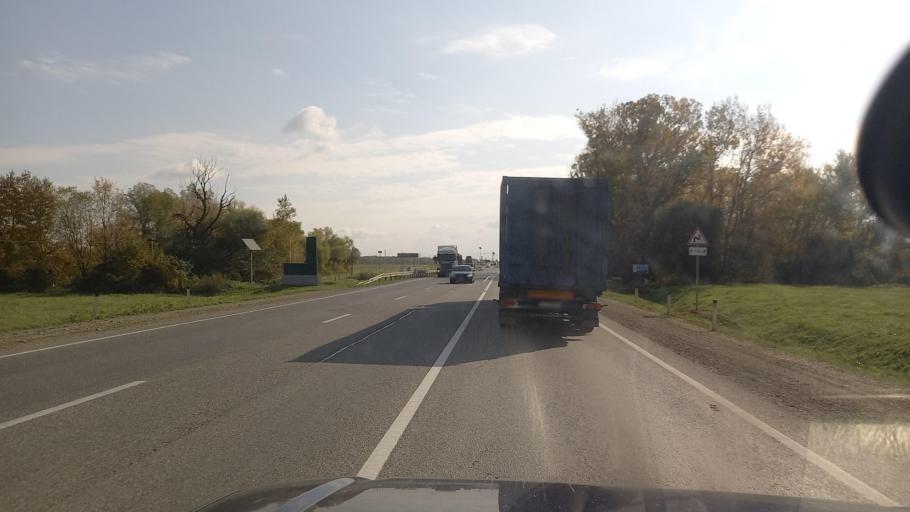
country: RU
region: Krasnodarskiy
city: Novoukrainskiy
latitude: 44.8858
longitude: 38.0848
